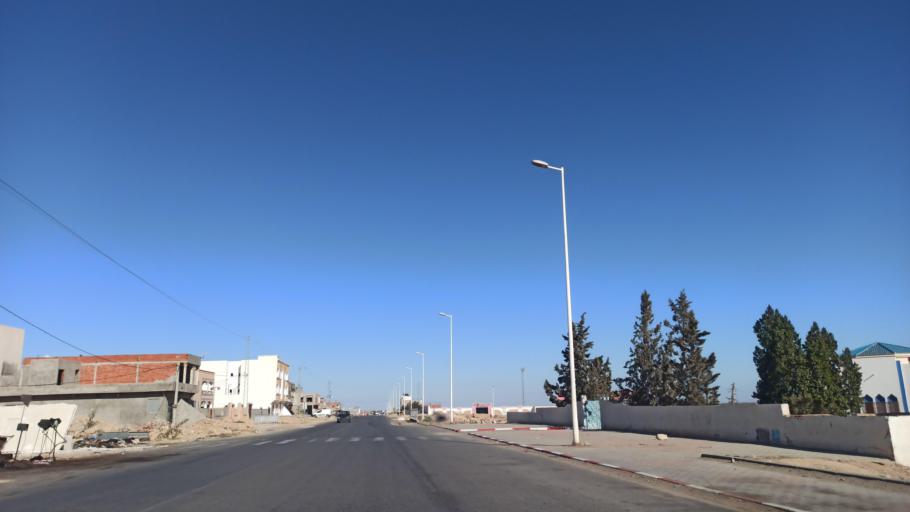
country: TN
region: Sidi Bu Zayd
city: Bi'r al Hufayy
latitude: 34.9408
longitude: 9.2032
